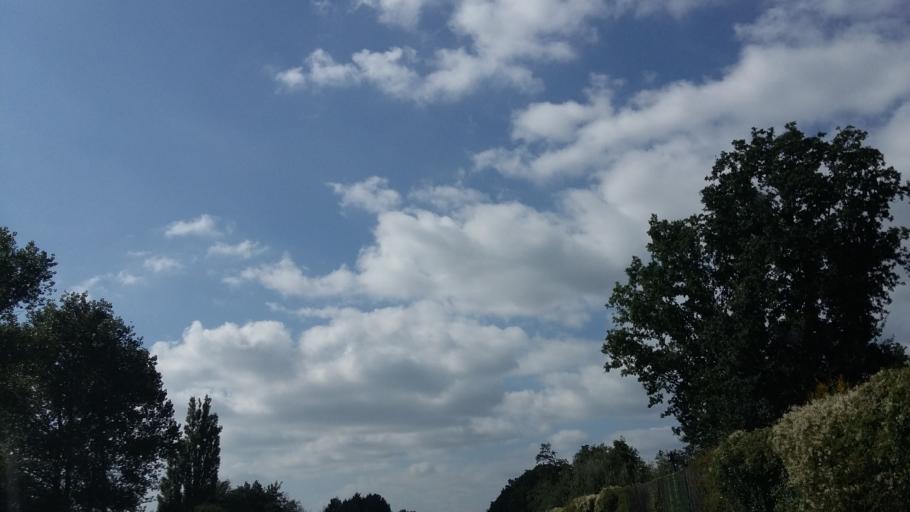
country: DE
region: Bremen
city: Bremen
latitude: 53.1242
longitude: 8.7788
